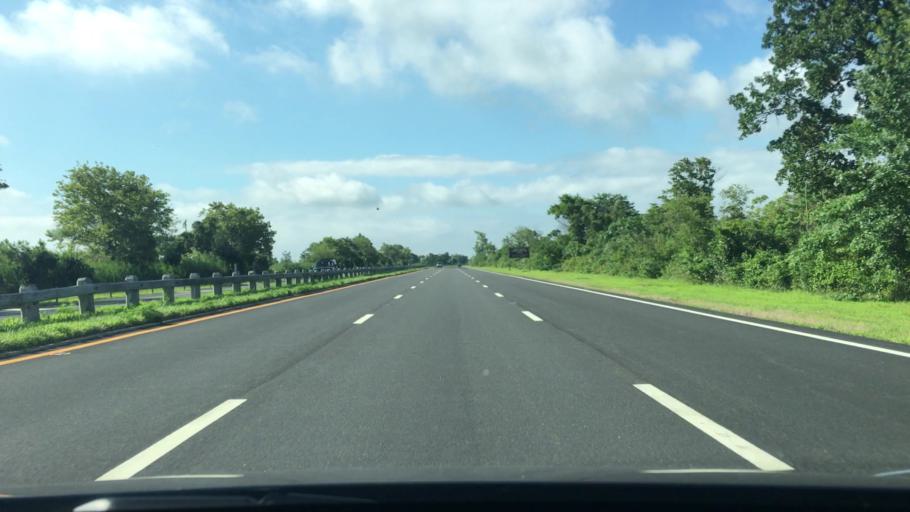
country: US
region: New York
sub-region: Nassau County
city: Bellmore
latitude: 40.6531
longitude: -73.5100
